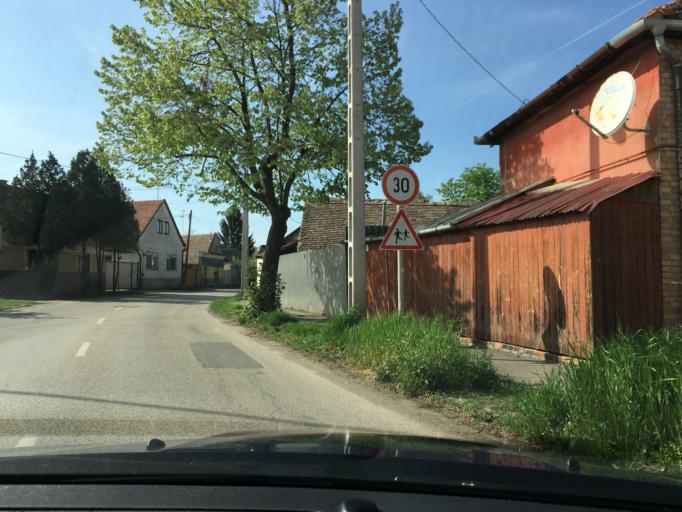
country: HU
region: Csongrad
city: Hodmezovasarhely
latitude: 46.4193
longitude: 20.3457
